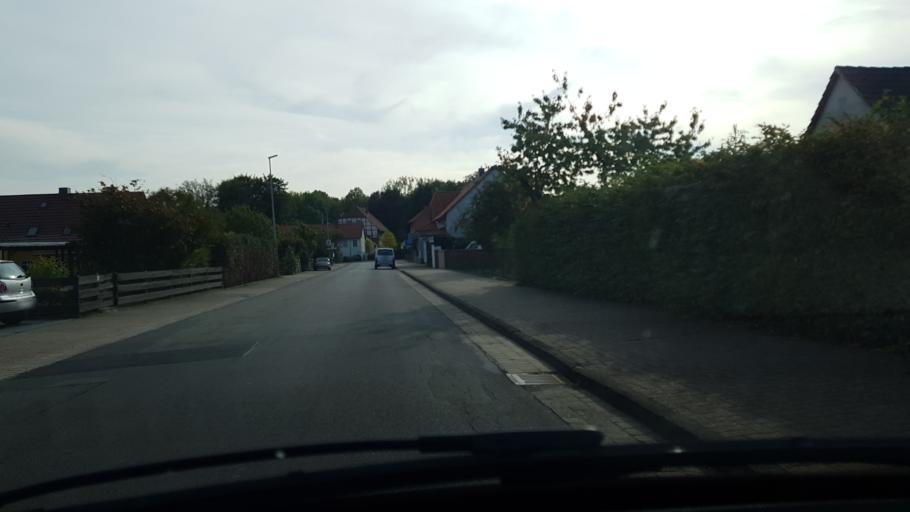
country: DE
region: Lower Saxony
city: Lehre
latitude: 52.3542
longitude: 10.6704
